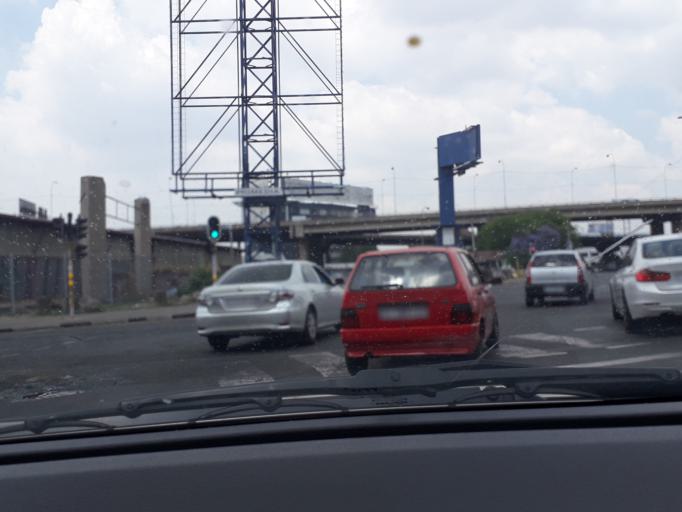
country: ZA
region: Gauteng
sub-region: City of Johannesburg Metropolitan Municipality
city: Johannesburg
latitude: -26.2116
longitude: 28.0444
